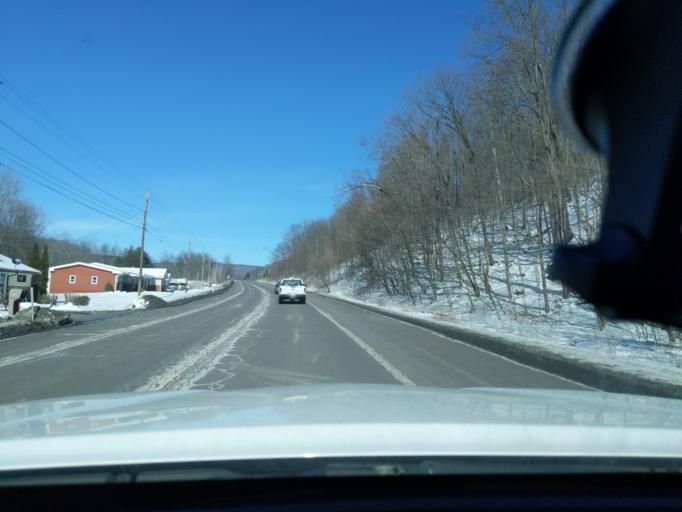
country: US
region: Maryland
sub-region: Allegany County
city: Westernport
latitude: 39.5145
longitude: -79.0208
